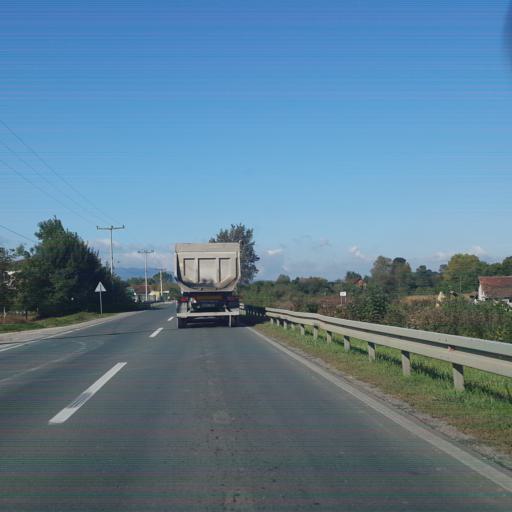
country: RS
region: Central Serbia
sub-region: Raski Okrug
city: Vrnjacka Banja
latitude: 43.6338
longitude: 20.9479
